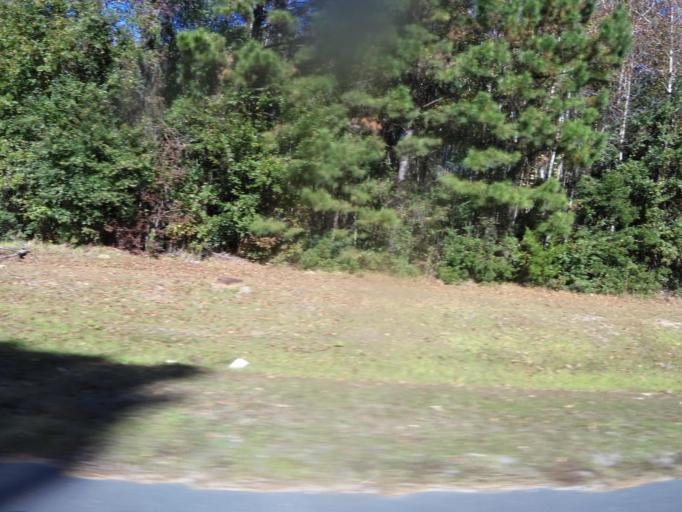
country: US
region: Georgia
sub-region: Liberty County
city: Midway
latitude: 31.7999
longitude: -81.4156
